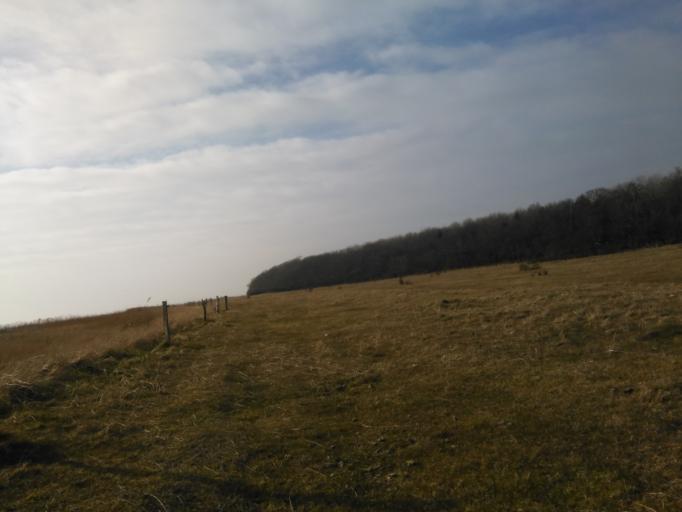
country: DK
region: Central Jutland
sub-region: Odder Kommune
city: Odder
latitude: 55.8382
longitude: 10.1900
